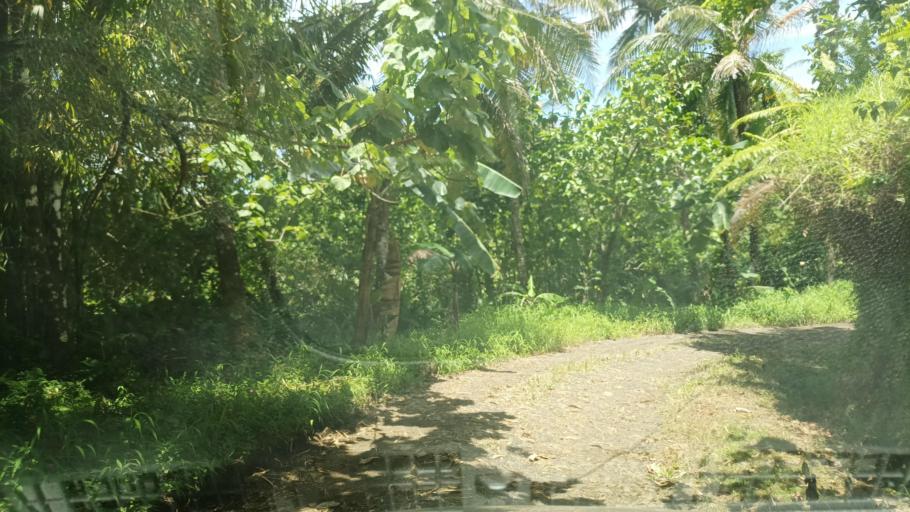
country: FM
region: Kosrae
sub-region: Malem Municipality
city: Malem
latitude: 5.2971
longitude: 163.0239
